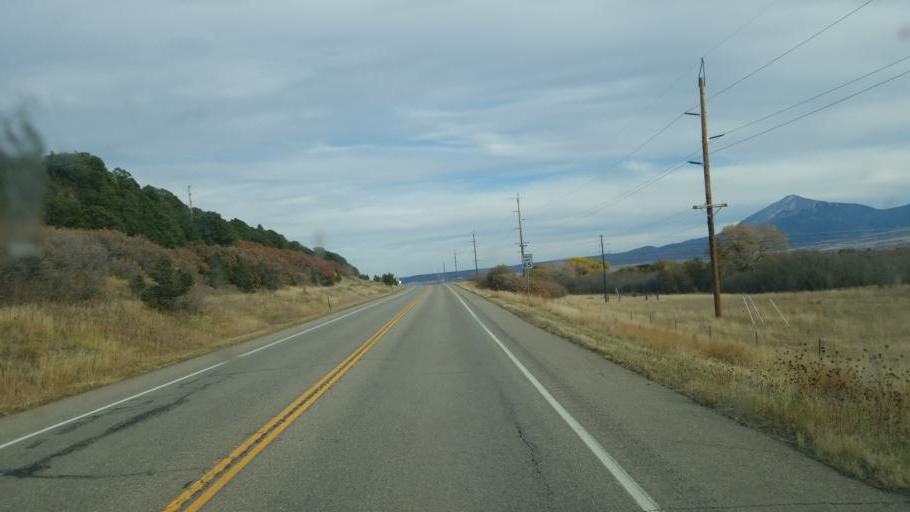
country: US
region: Colorado
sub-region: Huerfano County
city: Walsenburg
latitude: 37.5476
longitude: -105.0924
